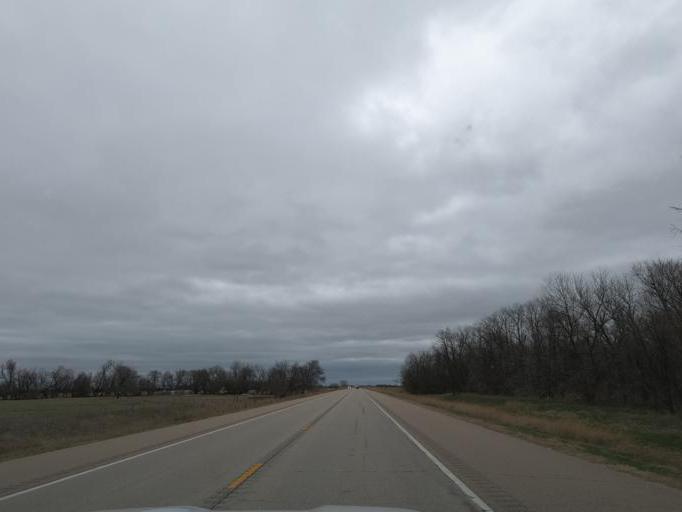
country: US
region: Kansas
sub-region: Stafford County
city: Stafford
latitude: 37.9699
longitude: -98.4034
